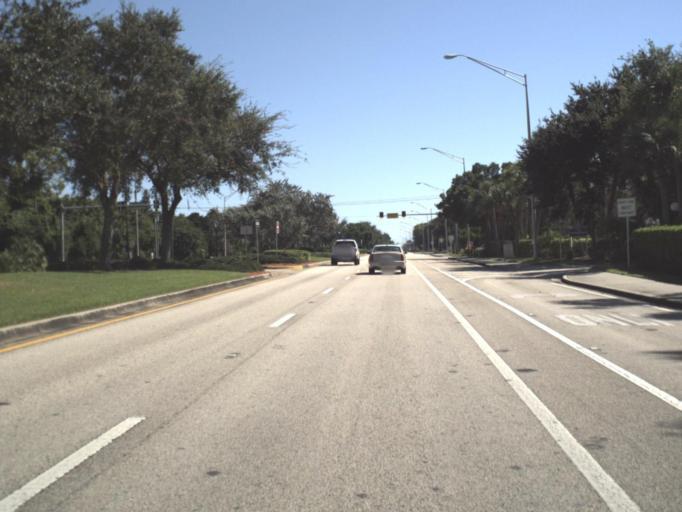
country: US
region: Florida
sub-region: Collier County
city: Naples
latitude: 26.1386
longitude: -81.7521
